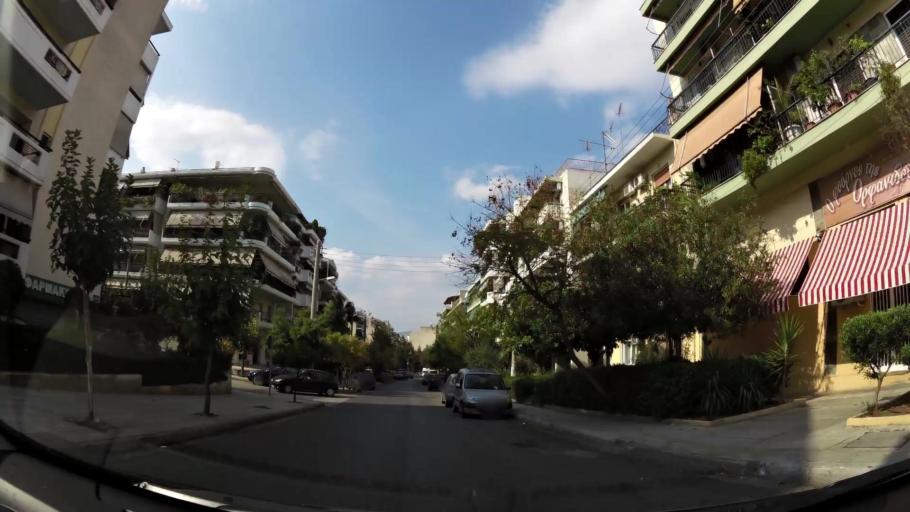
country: GR
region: Attica
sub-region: Nomarchia Athinas
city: Galatsi
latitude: 38.0223
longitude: 23.7413
